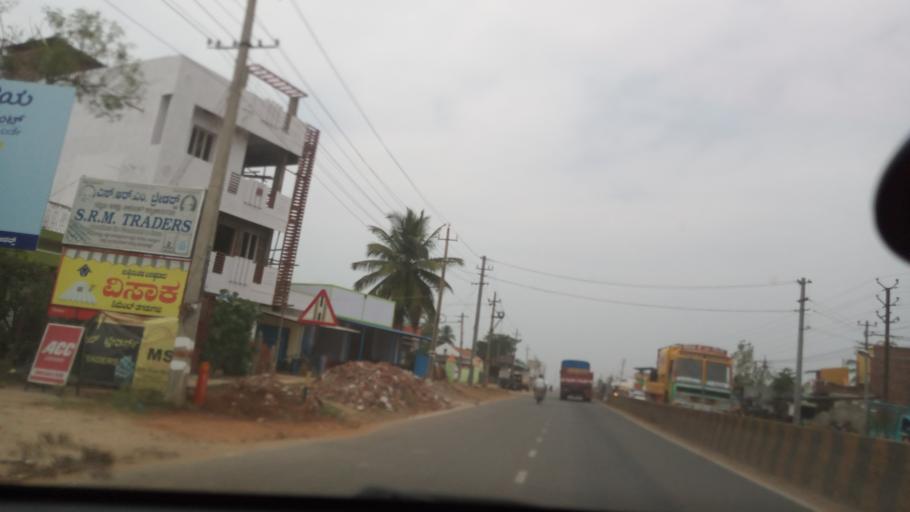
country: IN
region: Karnataka
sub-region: Chamrajnagar
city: Chamrajnagar
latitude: 11.9069
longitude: 76.9462
